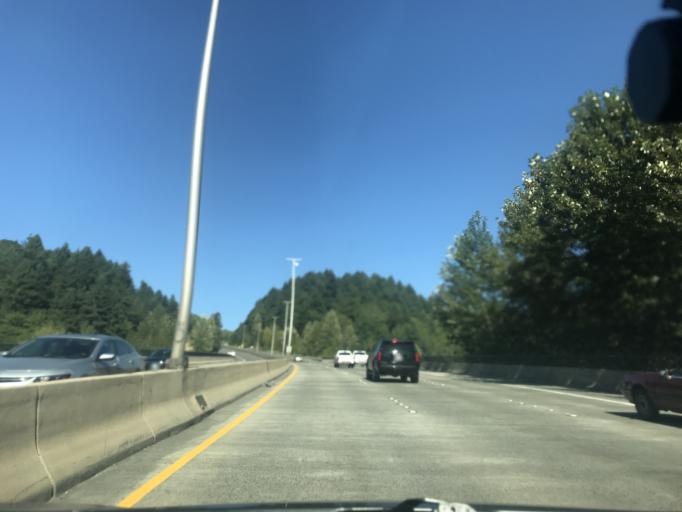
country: US
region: Washington
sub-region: King County
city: Kent
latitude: 47.3540
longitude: -122.2103
